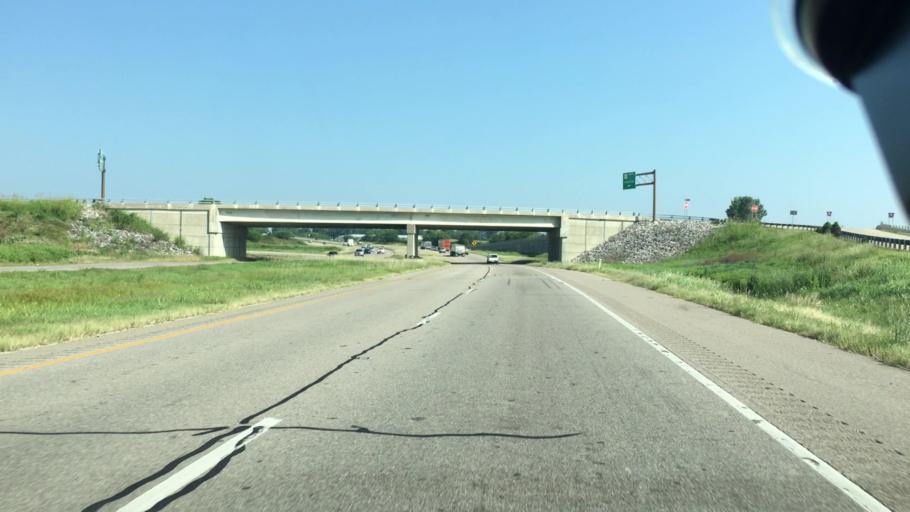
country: US
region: Indiana
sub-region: Gibson County
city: Princeton
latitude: 38.3115
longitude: -87.5680
